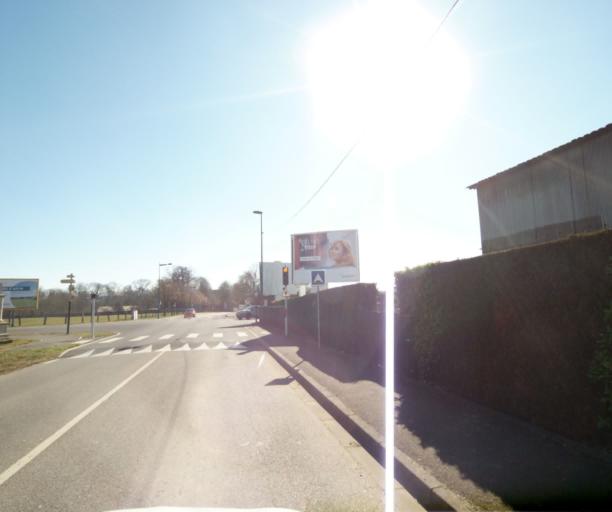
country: FR
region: Lorraine
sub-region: Departement de Meurthe-et-Moselle
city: Saulxures-les-Nancy
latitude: 48.6932
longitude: 6.2508
